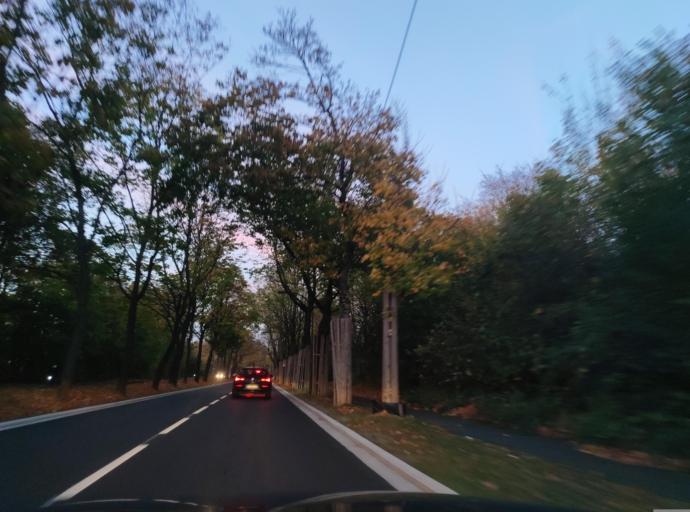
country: DE
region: North Rhine-Westphalia
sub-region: Regierungsbezirk Dusseldorf
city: Essen
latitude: 51.4281
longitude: 6.9639
